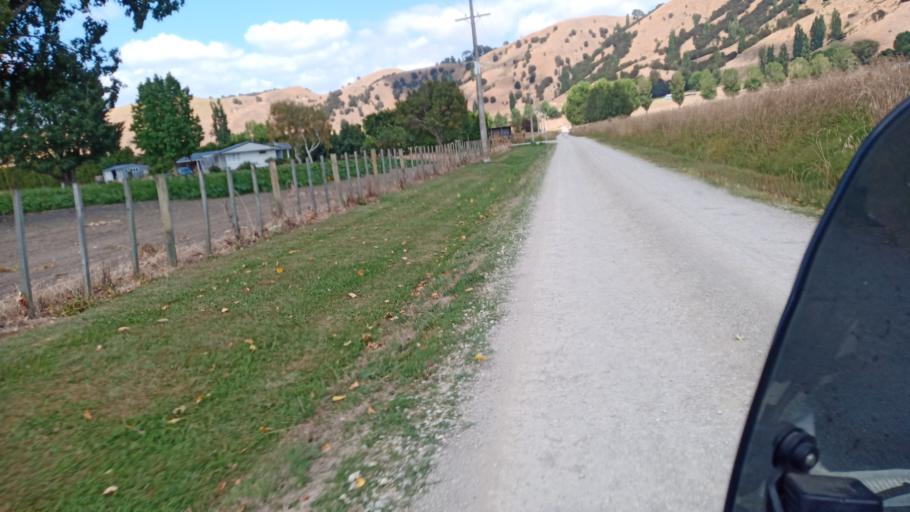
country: NZ
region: Gisborne
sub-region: Gisborne District
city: Gisborne
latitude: -38.4845
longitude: 177.8769
